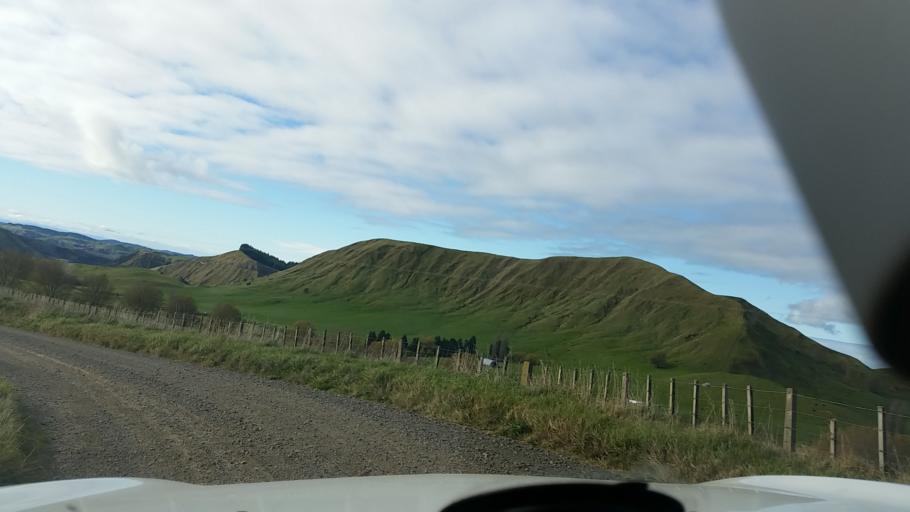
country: NZ
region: Hawke's Bay
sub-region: Napier City
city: Napier
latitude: -39.1247
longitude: 176.9170
